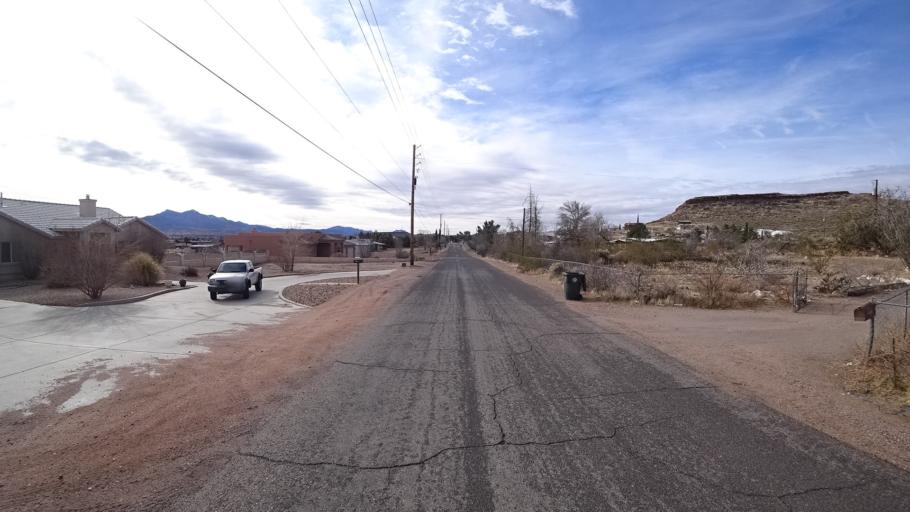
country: US
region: Arizona
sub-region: Mohave County
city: Kingman
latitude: 35.2277
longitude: -114.0469
